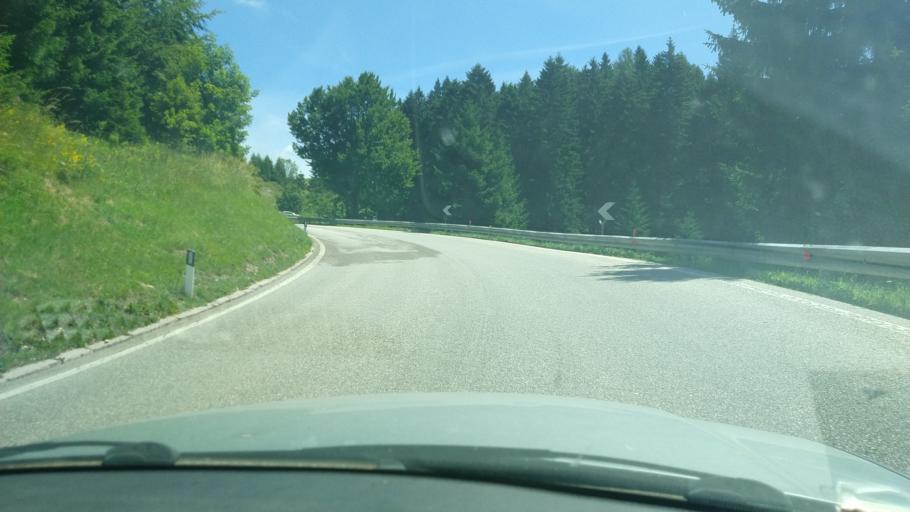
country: IT
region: Trentino-Alto Adige
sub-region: Provincia di Trento
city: Folgaria
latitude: 45.9181
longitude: 11.2011
